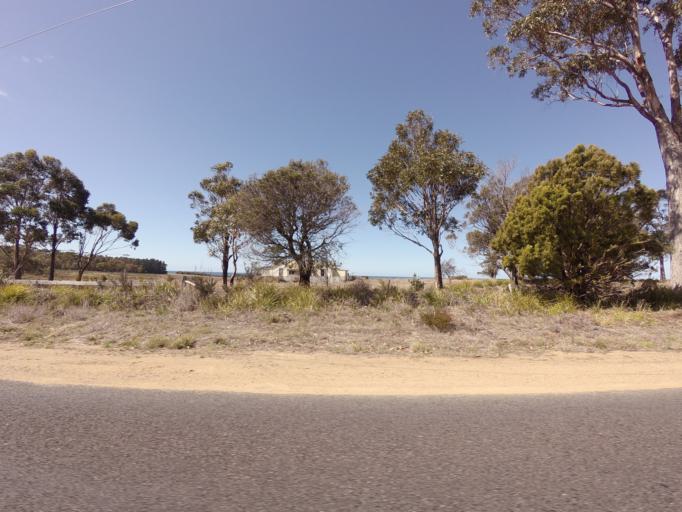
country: AU
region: Tasmania
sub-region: Break O'Day
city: St Helens
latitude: -41.6997
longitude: 148.2760
